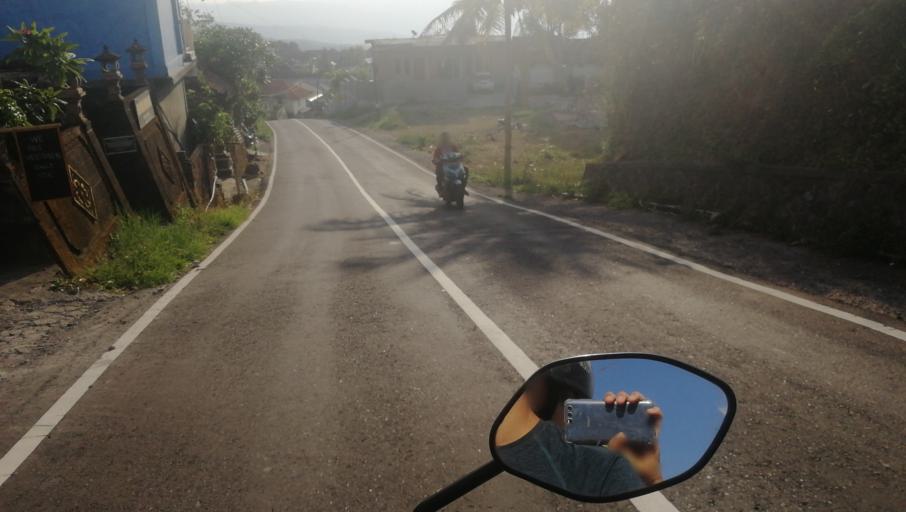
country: ID
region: Bali
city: Munduk
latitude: -8.2655
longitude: 115.0581
